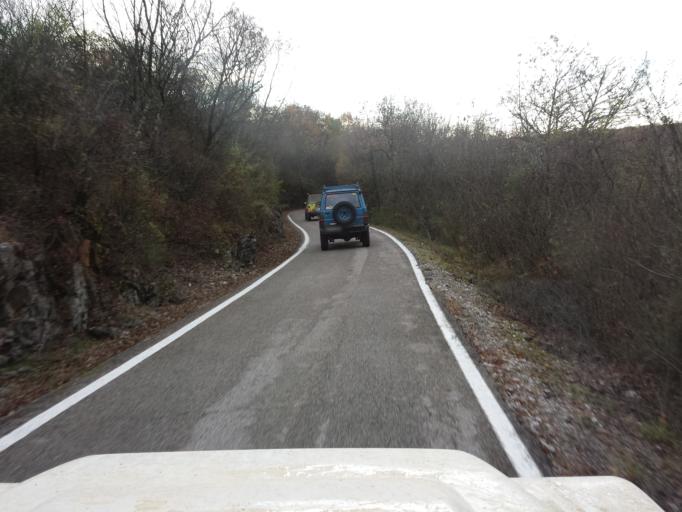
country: IT
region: Friuli Venezia Giulia
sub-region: Provincia di Gorizia
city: Farra d'Isonzo
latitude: 45.8797
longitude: 13.5329
